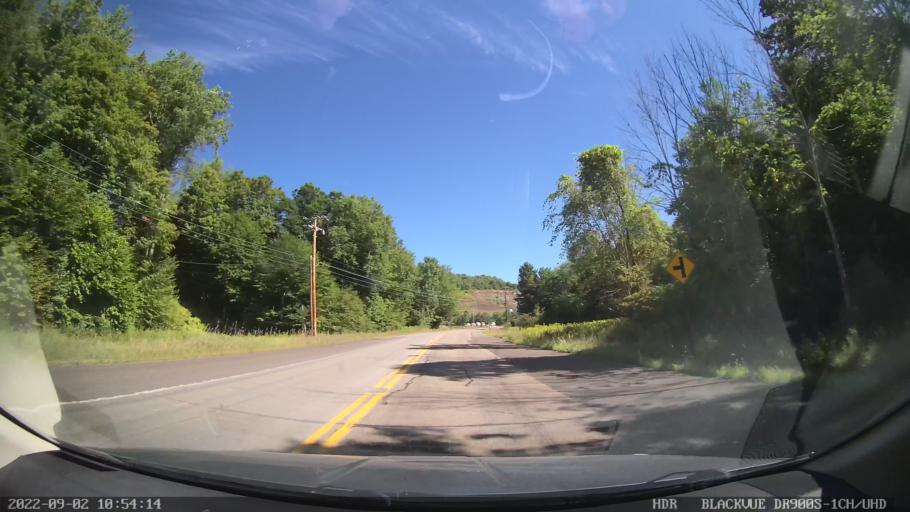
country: US
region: Pennsylvania
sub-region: Tioga County
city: Blossburg
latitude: 41.6568
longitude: -77.0937
